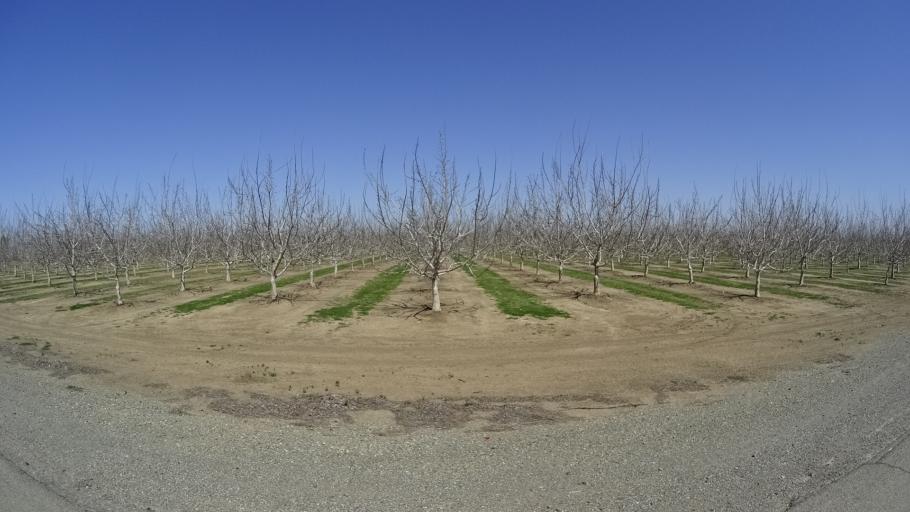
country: US
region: California
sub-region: Butte County
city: Durham
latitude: 39.4642
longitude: -121.9403
